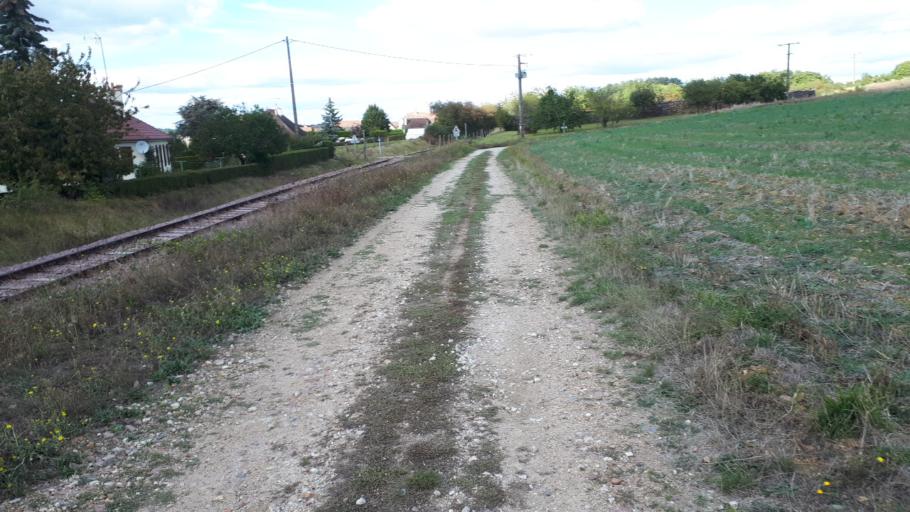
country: FR
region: Centre
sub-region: Departement du Loir-et-Cher
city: Villiers-sur-Loir
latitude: 47.7800
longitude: 0.9638
